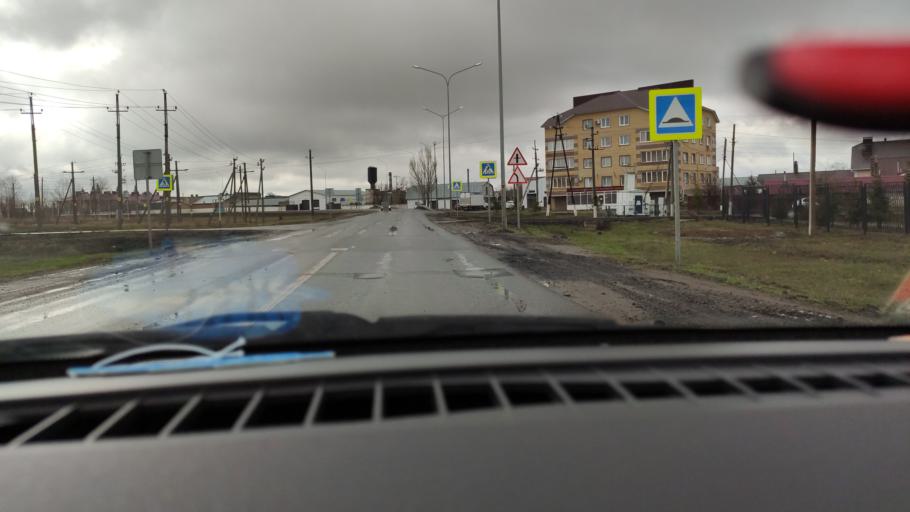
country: RU
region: Tatarstan
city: Nurlat
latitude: 54.4322
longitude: 50.8172
